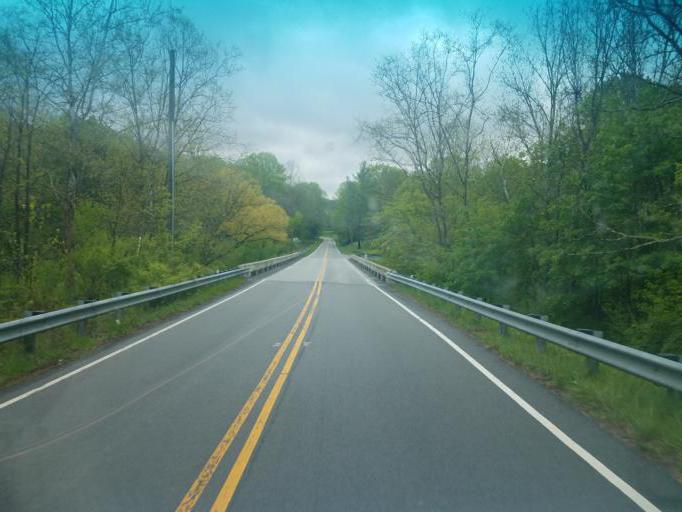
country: US
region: Virginia
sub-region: Washington County
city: Emory
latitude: 36.6572
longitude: -81.8034
